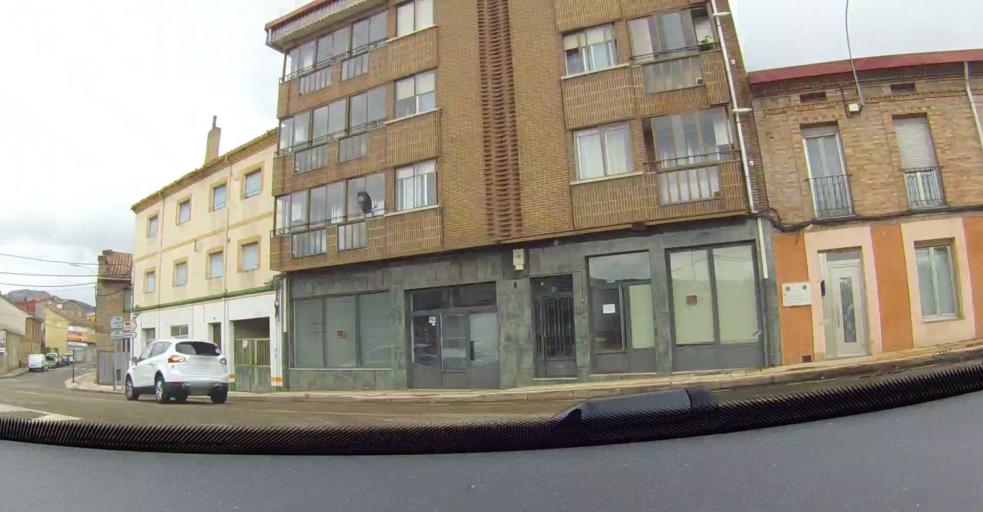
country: ES
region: Castille and Leon
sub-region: Provincia de Leon
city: Cistierna
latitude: 42.8005
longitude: -5.1254
